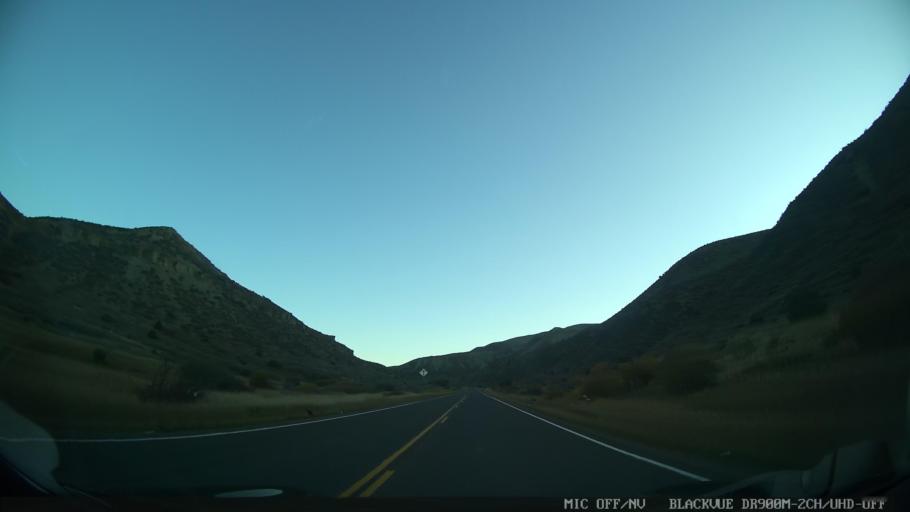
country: US
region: Colorado
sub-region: Eagle County
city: Edwards
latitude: 39.7757
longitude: -106.6829
